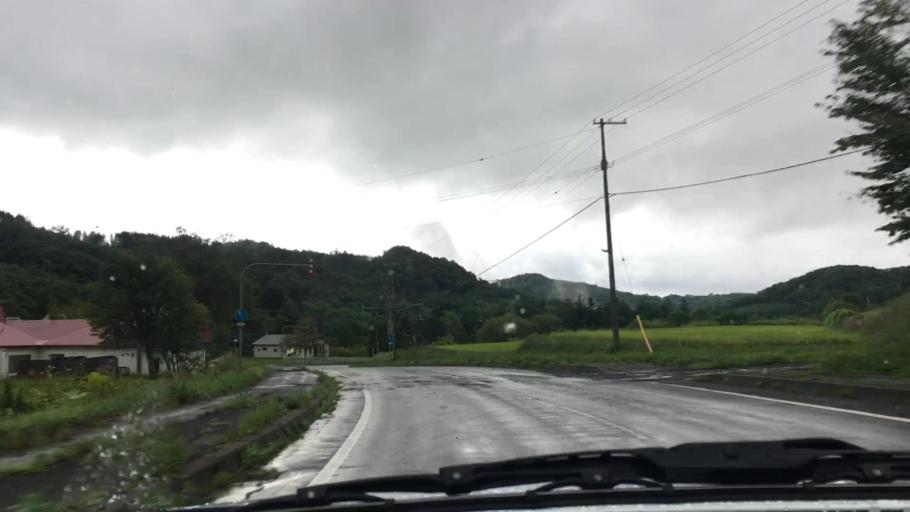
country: JP
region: Hokkaido
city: Niseko Town
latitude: 42.6522
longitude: 140.7388
